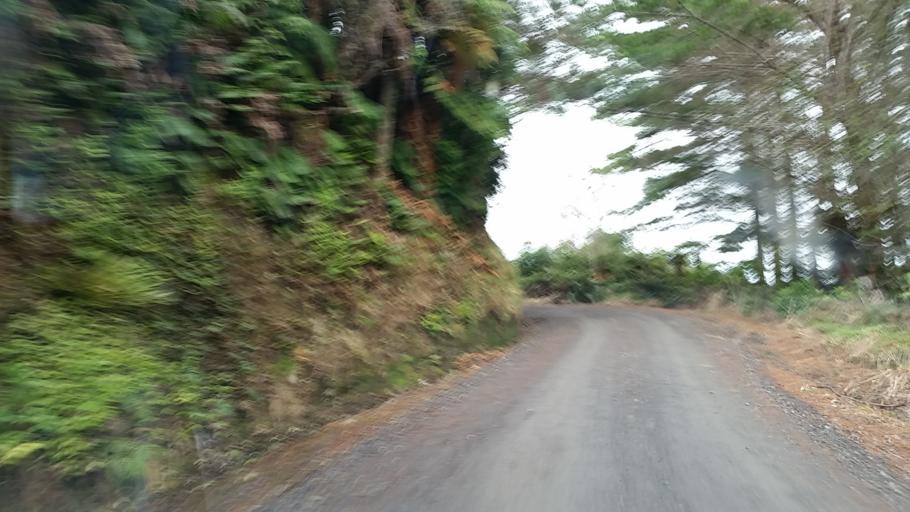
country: NZ
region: Taranaki
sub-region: New Plymouth District
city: Waitara
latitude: -39.1623
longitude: 174.5423
